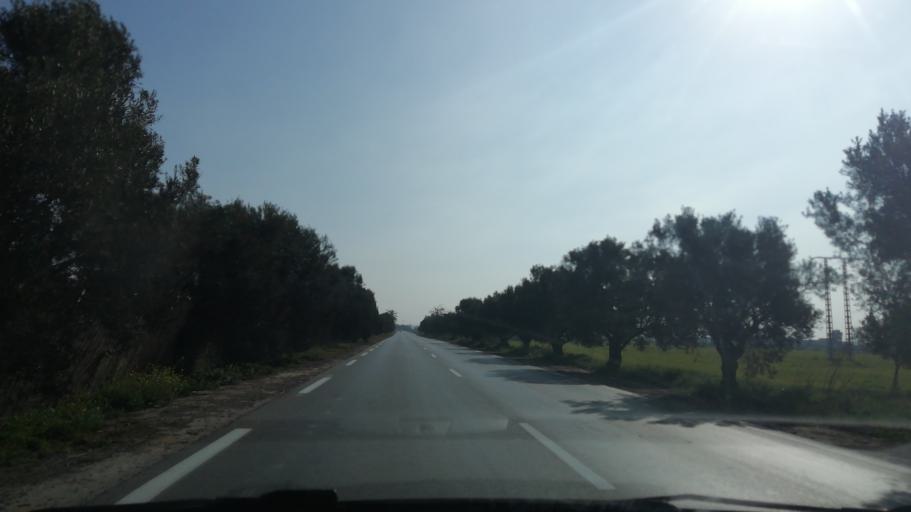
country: DZ
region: Mostaganem
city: Mostaganem
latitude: 35.7420
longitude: -0.0033
